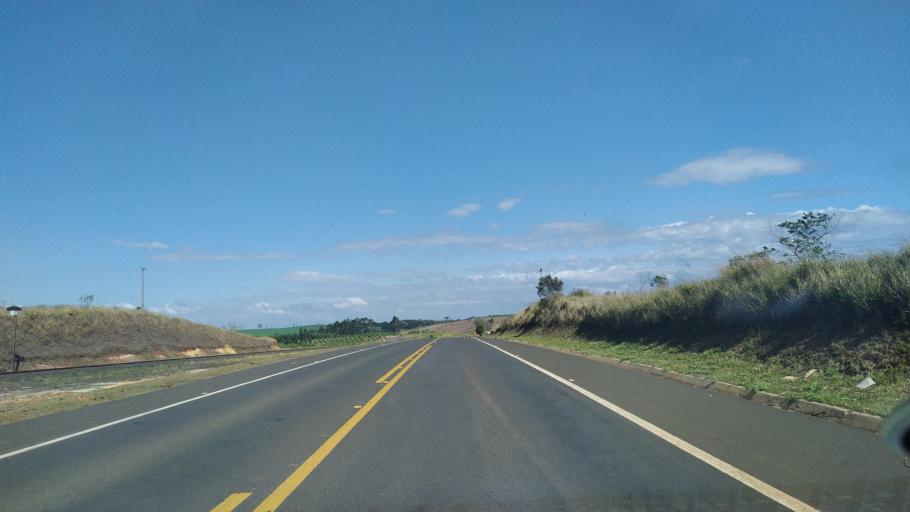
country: BR
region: Parana
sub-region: Ortigueira
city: Ortigueira
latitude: -24.2774
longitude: -50.8071
